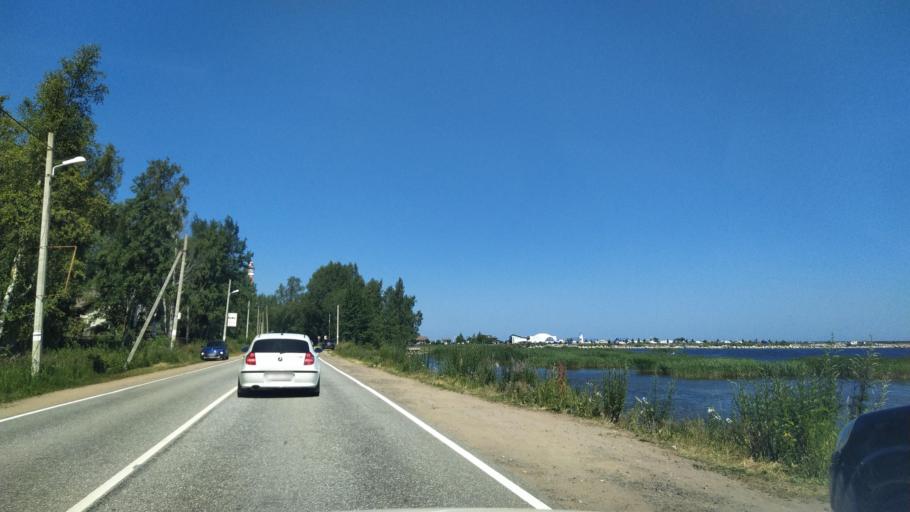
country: RU
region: Leningrad
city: Borisova Griva
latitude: 60.1134
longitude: 31.0840
